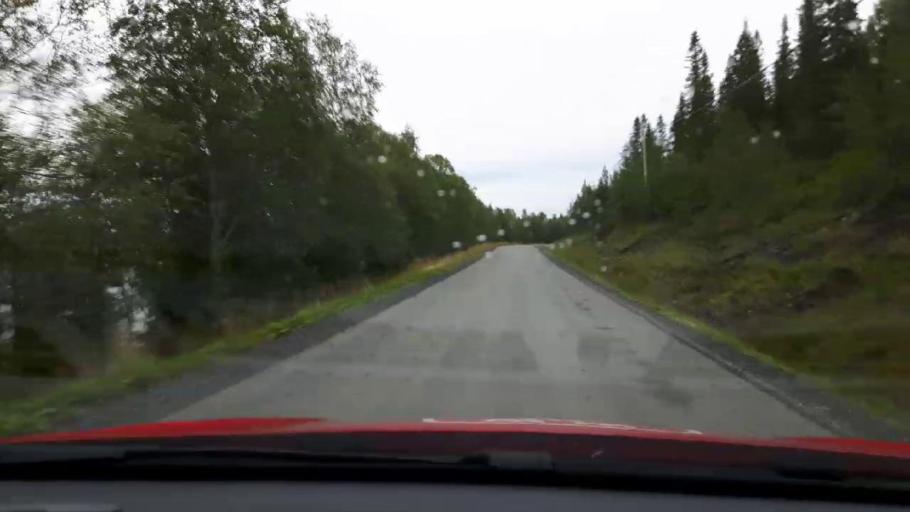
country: SE
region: Jaemtland
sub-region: Are Kommun
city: Are
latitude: 63.4802
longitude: 13.1533
